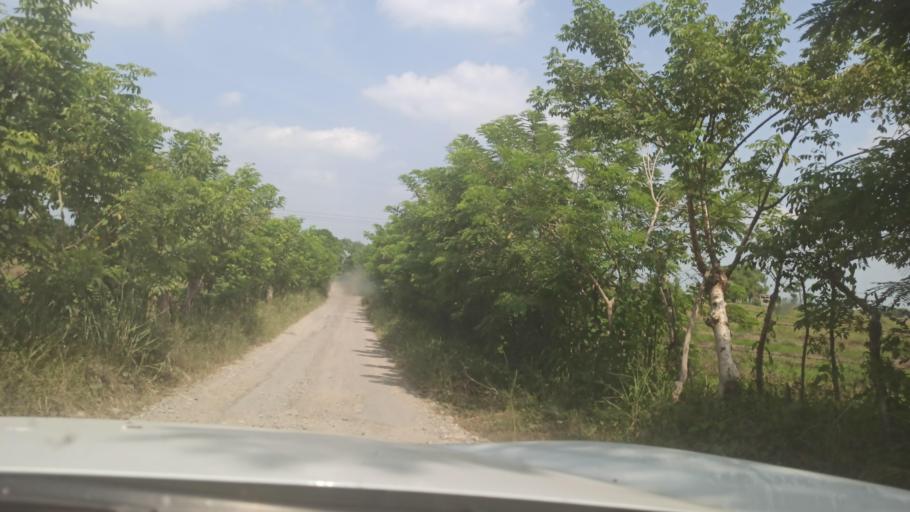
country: MX
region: Veracruz
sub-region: Atzalan
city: Colonias Pedernales
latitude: 20.0428
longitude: -97.0053
